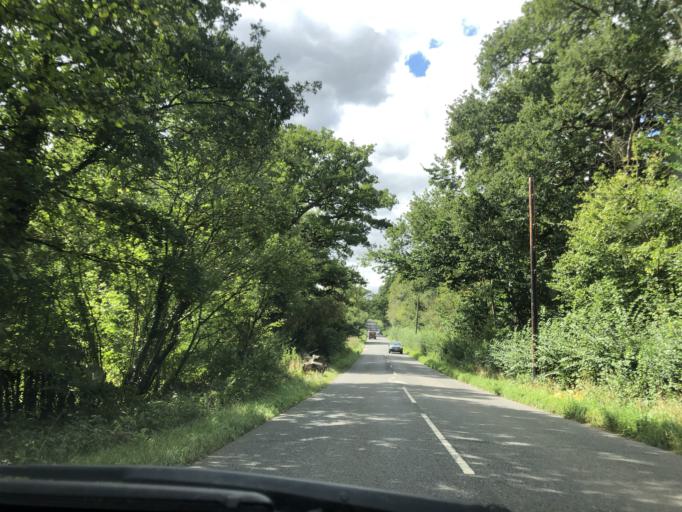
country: GB
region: England
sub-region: Kent
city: Halstead
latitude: 51.2914
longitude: 0.1362
